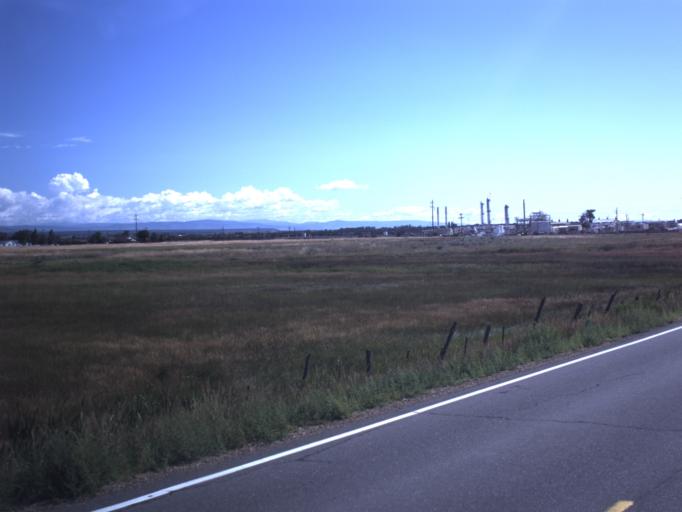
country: US
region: Utah
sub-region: Duchesne County
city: Duchesne
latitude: 40.3556
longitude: -110.3358
